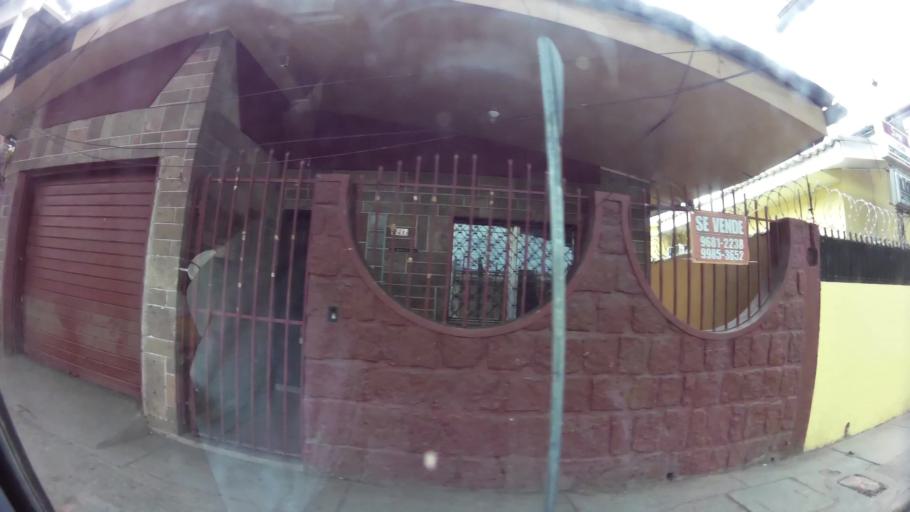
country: HN
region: Francisco Morazan
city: Tegucigalpa
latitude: 14.0858
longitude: -87.2035
